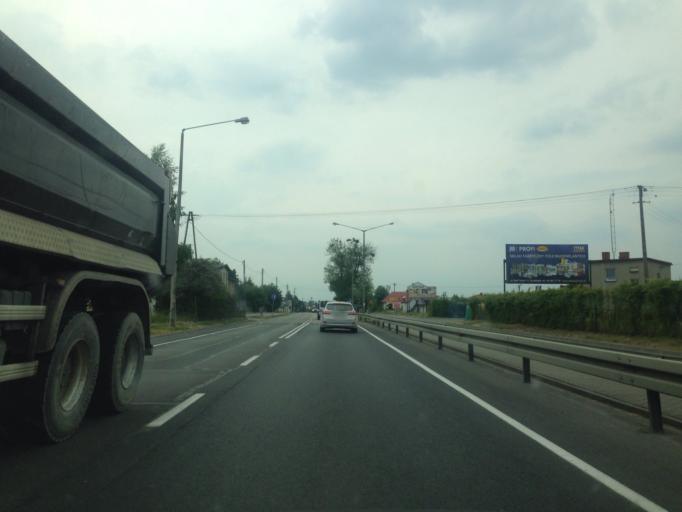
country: PL
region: Kujawsko-Pomorskie
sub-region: Grudziadz
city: Grudziadz
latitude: 53.5060
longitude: 18.8239
